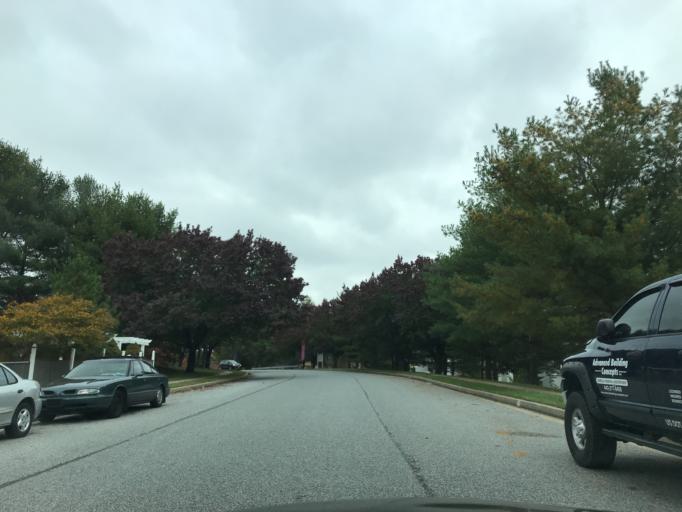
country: US
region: Maryland
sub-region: Baltimore County
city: Carney
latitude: 39.3864
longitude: -76.5126
